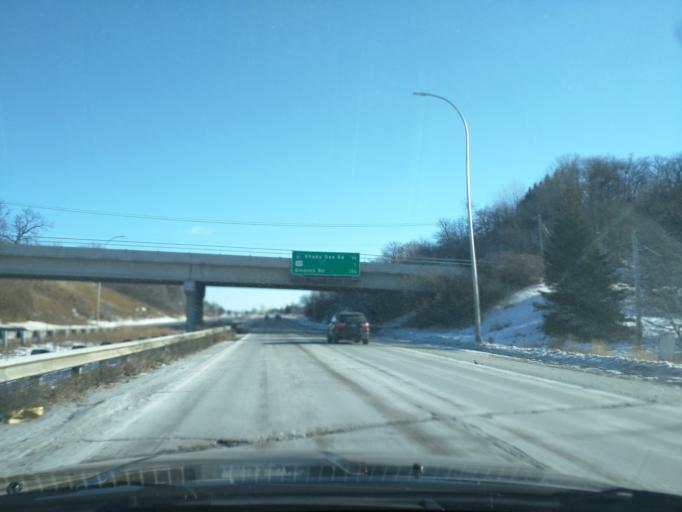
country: US
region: Minnesota
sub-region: Hennepin County
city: Hopkins
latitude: 44.8920
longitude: -93.4337
